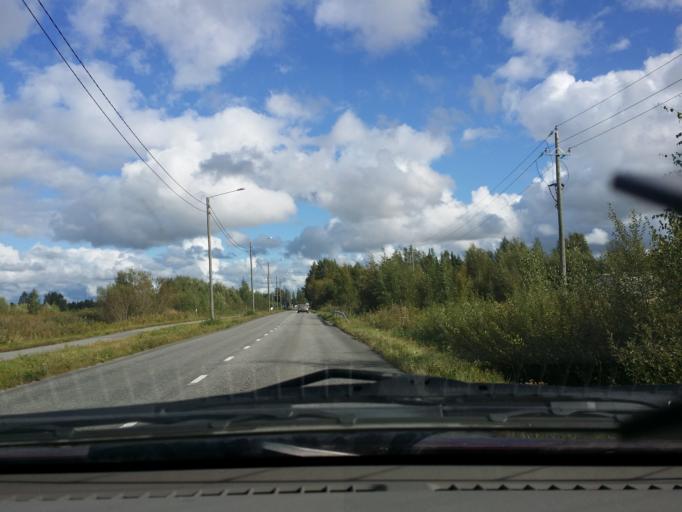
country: FI
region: Satakunta
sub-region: Pori
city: Pori
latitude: 61.4939
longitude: 21.8314
